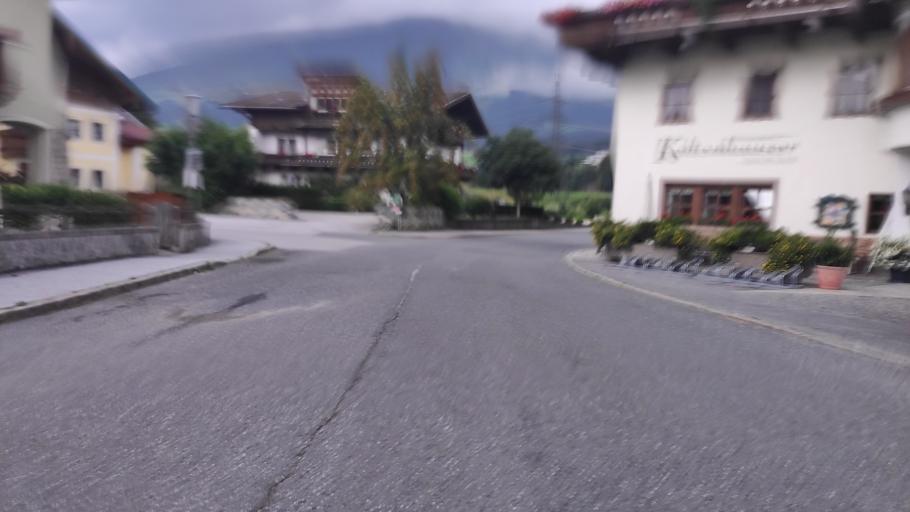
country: AT
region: Salzburg
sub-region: Politischer Bezirk Zell am See
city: Hollersbach im Pinzgau
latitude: 47.2759
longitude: 12.4192
